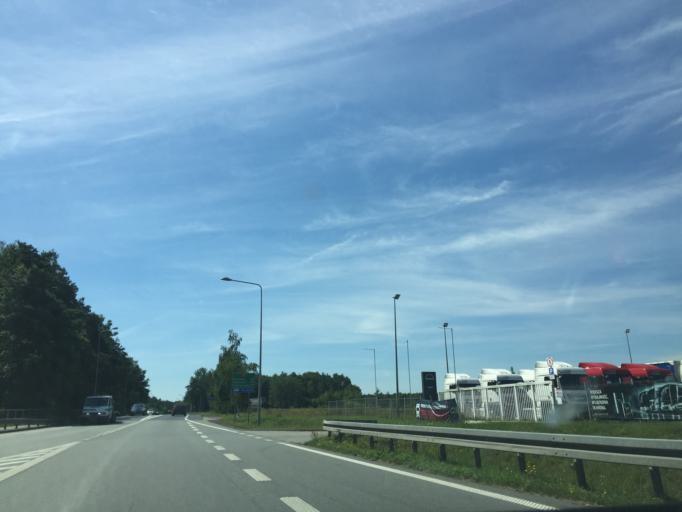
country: PL
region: Lodz Voivodeship
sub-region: Piotrkow Trybunalski
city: Piotrkow Trybunalski
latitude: 51.4405
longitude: 19.7218
